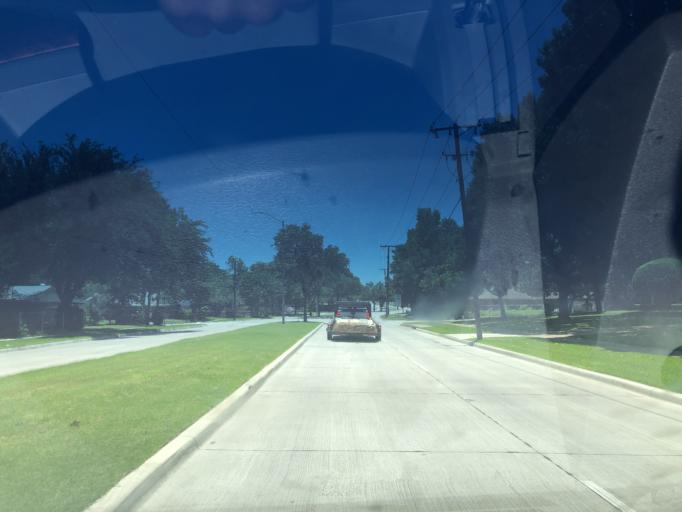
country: US
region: Texas
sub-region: Dallas County
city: Grand Prairie
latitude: 32.7166
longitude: -97.0150
